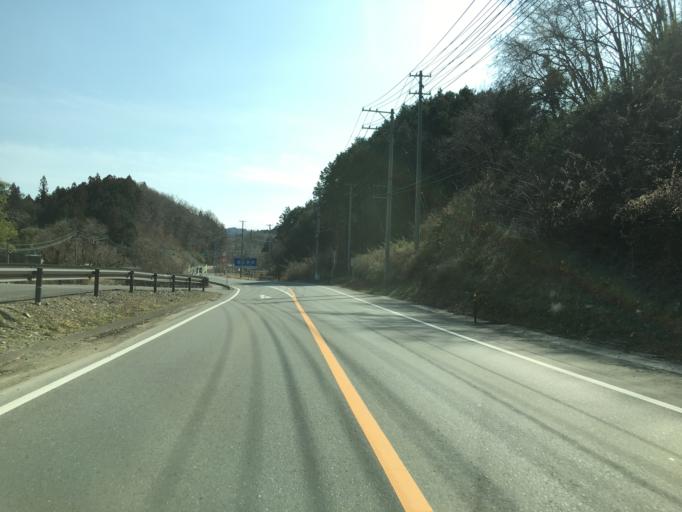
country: JP
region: Ibaraki
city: Daigo
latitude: 36.8552
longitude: 140.4299
